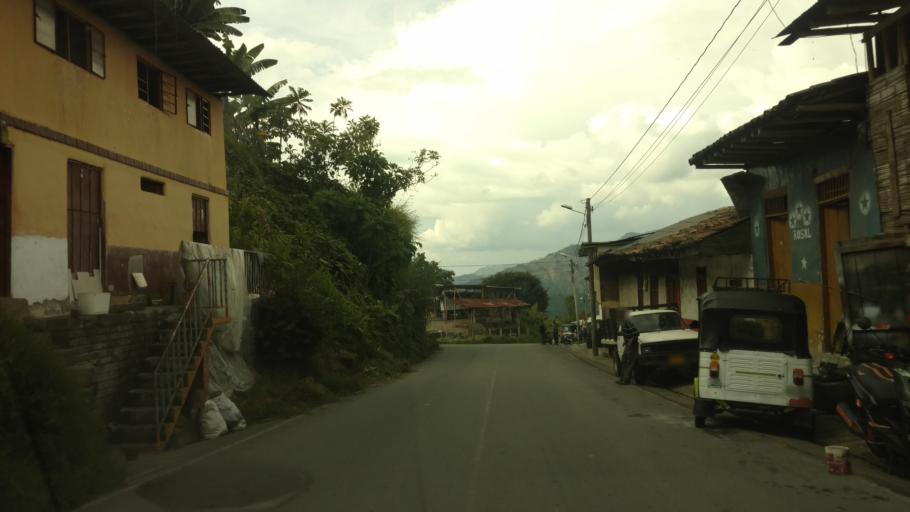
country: CO
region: Caldas
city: Neira
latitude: 5.1682
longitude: -75.5184
